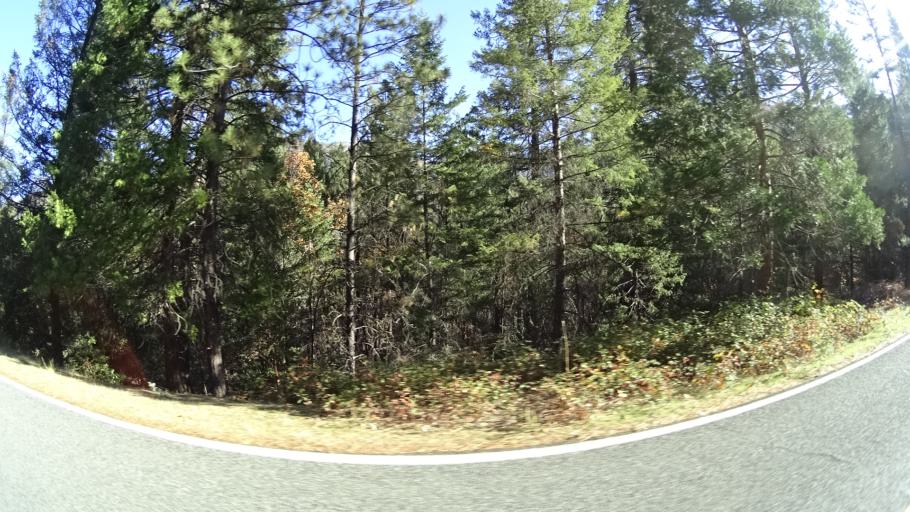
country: US
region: California
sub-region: Siskiyou County
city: Yreka
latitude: 41.8933
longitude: -122.8242
